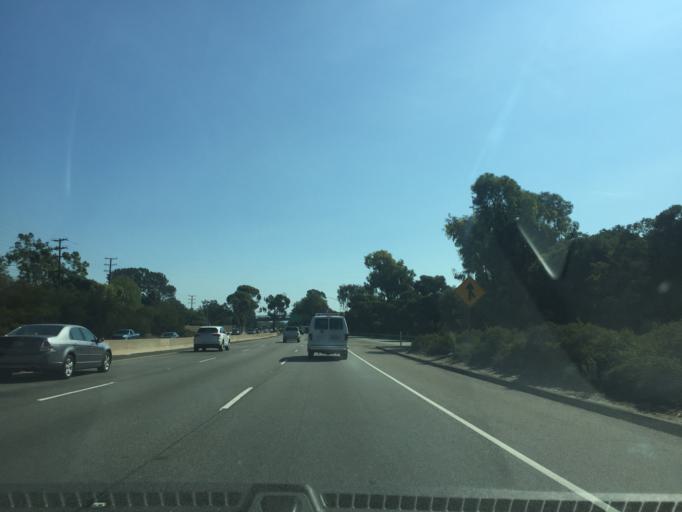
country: US
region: California
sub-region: Santa Barbara County
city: Mission Canyon
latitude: 34.4275
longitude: -119.7314
